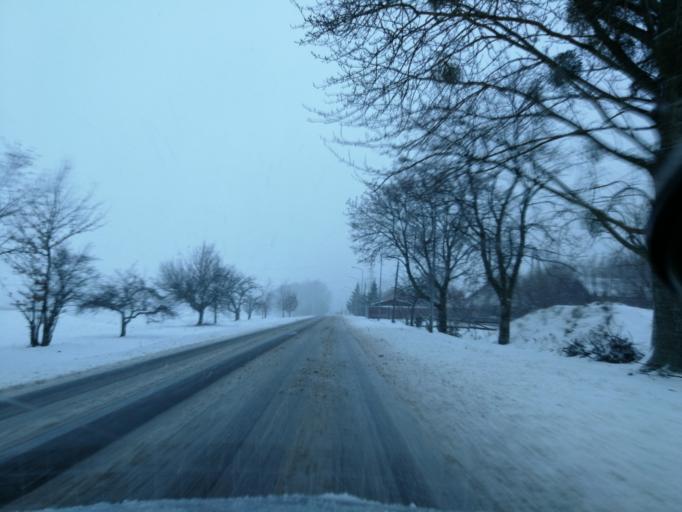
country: PL
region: Silesian Voivodeship
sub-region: Powiat pszczynski
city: Radostowice
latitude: 49.9960
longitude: 18.8979
